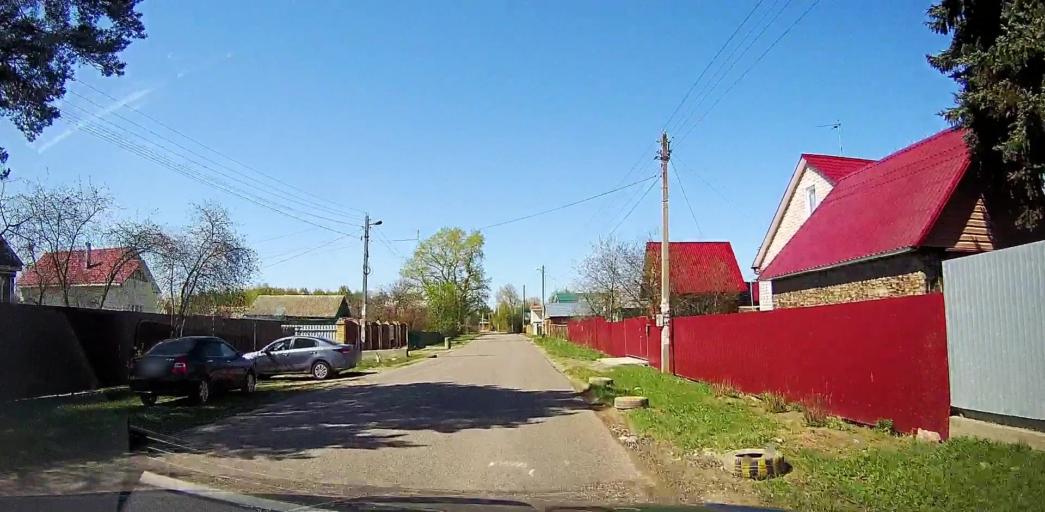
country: RU
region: Moskovskaya
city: Malyshevo
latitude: 55.4587
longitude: 38.3692
